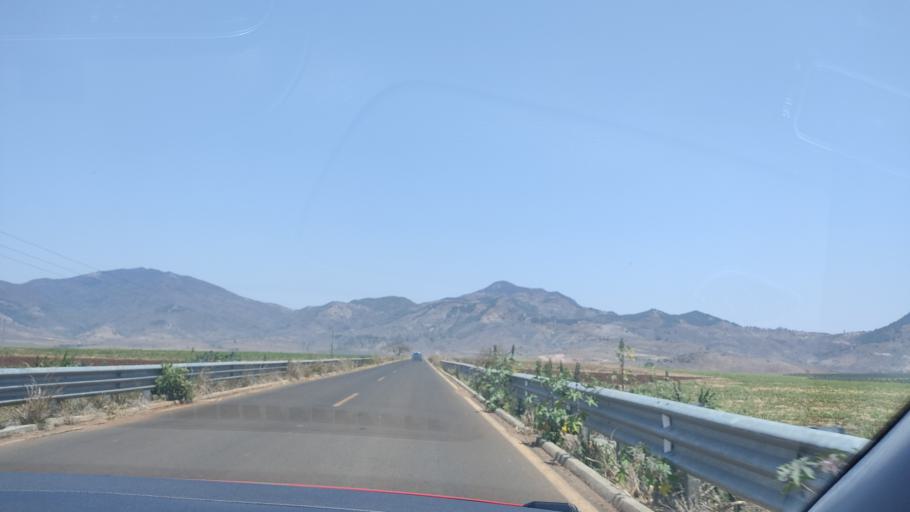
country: MX
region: Nayarit
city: Puga
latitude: 21.5951
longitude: -104.7407
